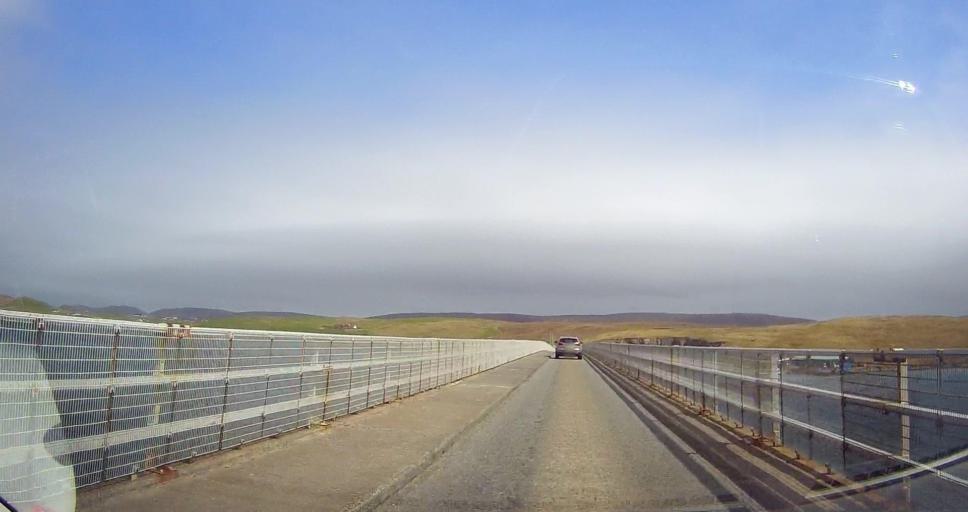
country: GB
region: Scotland
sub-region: Shetland Islands
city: Sandwick
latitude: 60.1052
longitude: -1.3103
